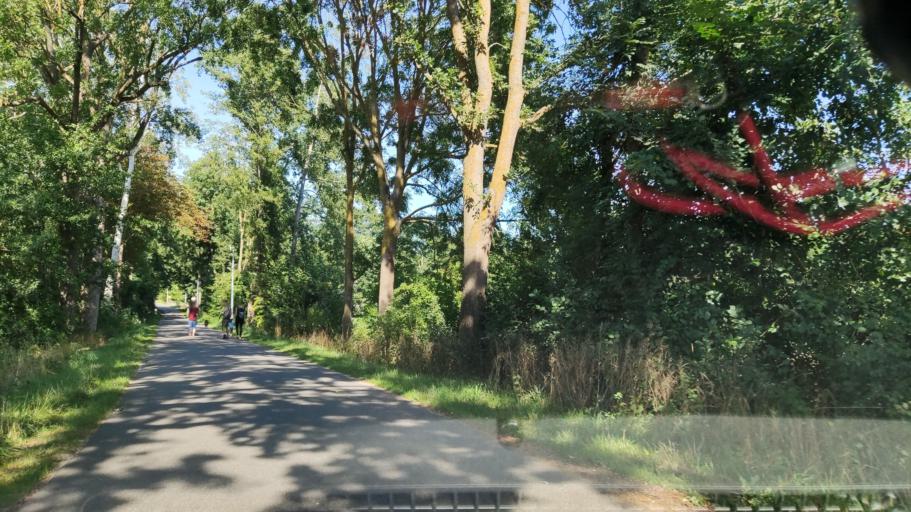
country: DE
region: Lower Saxony
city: Hitzacker
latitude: 53.1486
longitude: 10.9889
